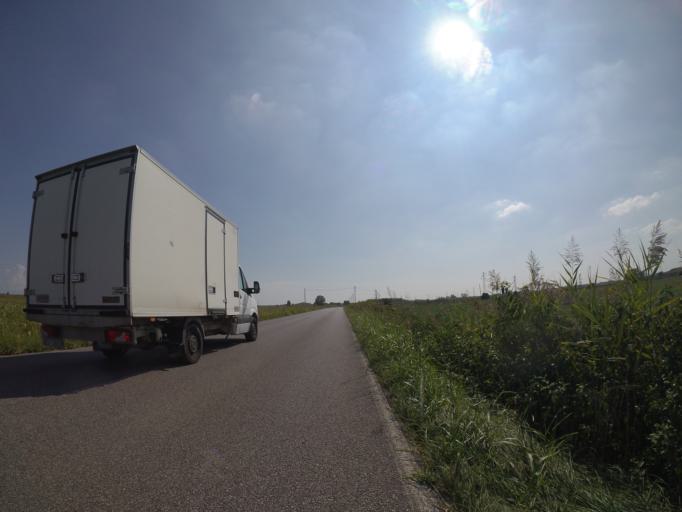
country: IT
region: Friuli Venezia Giulia
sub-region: Provincia di Udine
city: Pocenia
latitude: 45.8201
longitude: 13.1013
